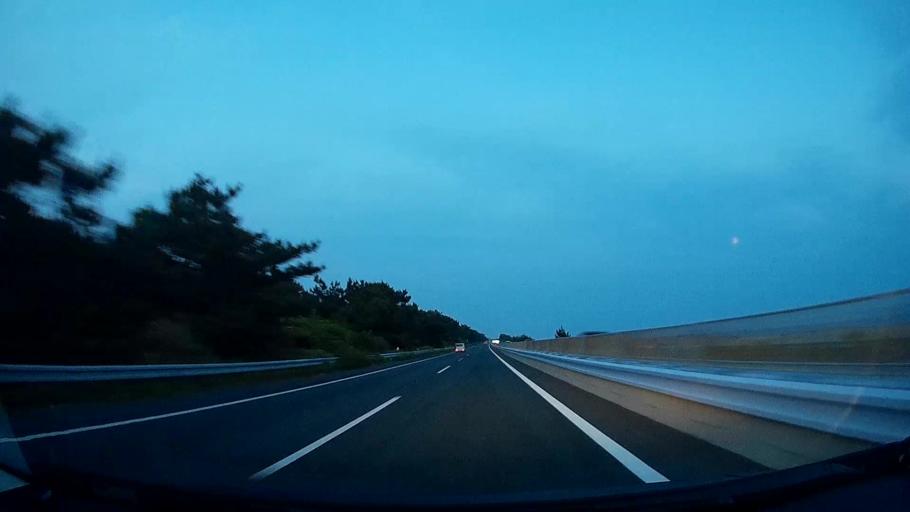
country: JP
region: Shizuoka
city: Kosai-shi
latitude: 34.6784
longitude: 137.6098
